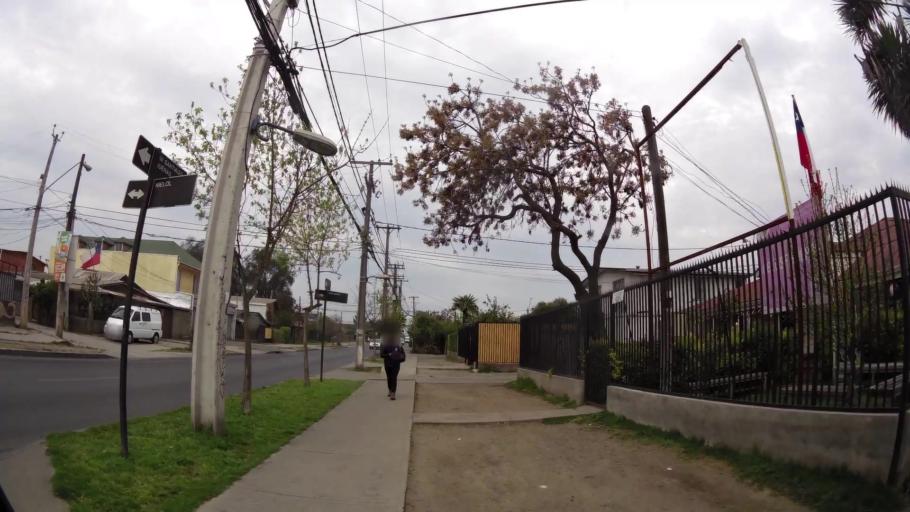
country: CL
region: Santiago Metropolitan
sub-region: Provincia de Santiago
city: Lo Prado
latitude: -33.4963
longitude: -70.7630
